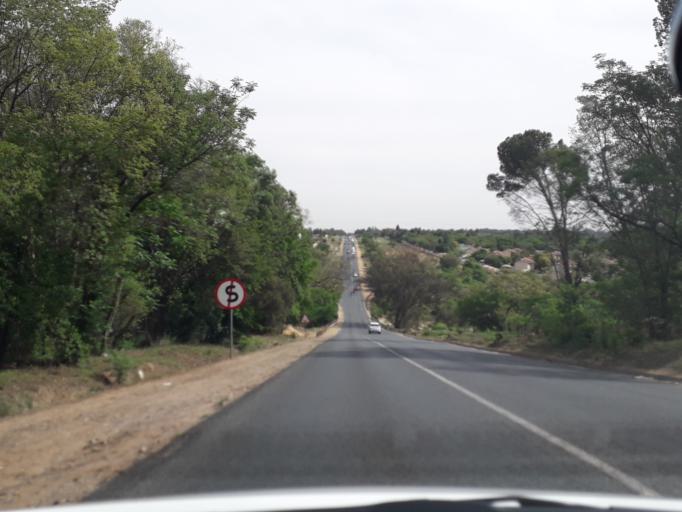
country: ZA
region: Gauteng
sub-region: City of Johannesburg Metropolitan Municipality
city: Diepsloot
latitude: -26.0078
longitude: 28.0387
